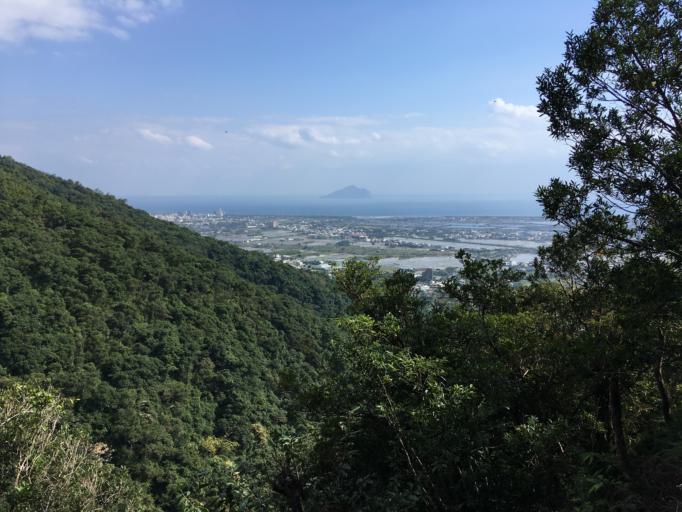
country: TW
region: Taiwan
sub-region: Yilan
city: Yilan
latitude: 24.8442
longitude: 121.7778
